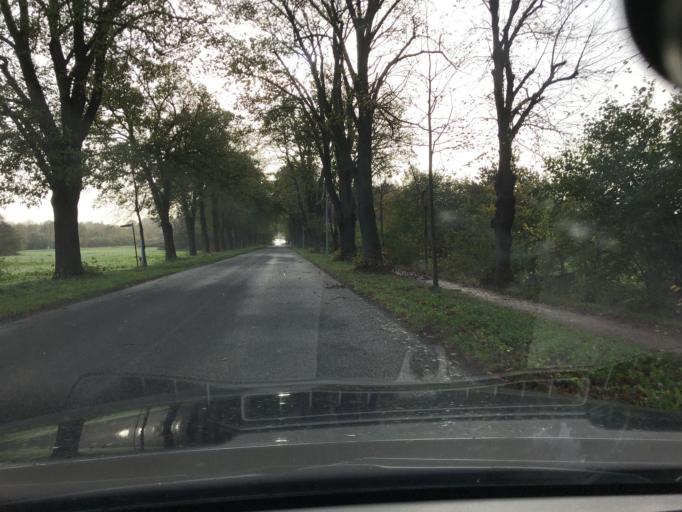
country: DE
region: Lower Saxony
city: Syke
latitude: 52.9445
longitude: 8.8206
